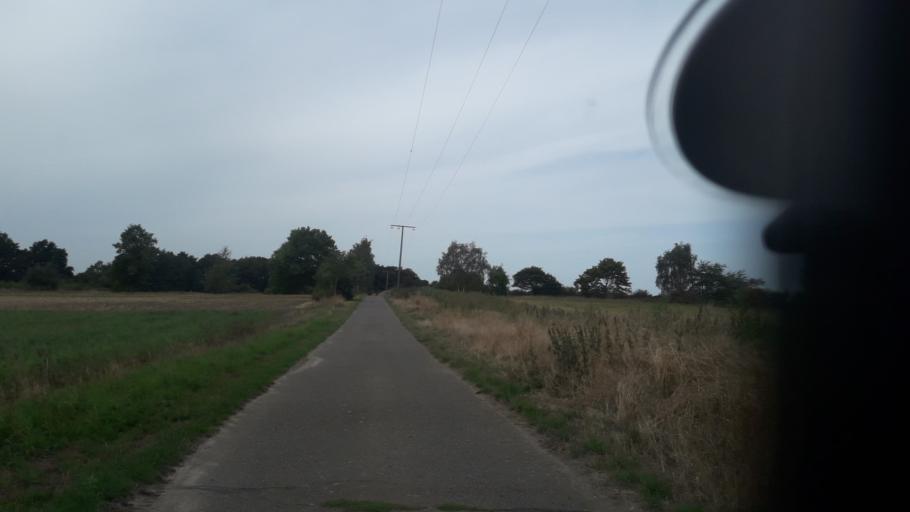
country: DE
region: Lower Saxony
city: Gross Twulpstedt
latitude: 52.3580
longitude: 10.9177
